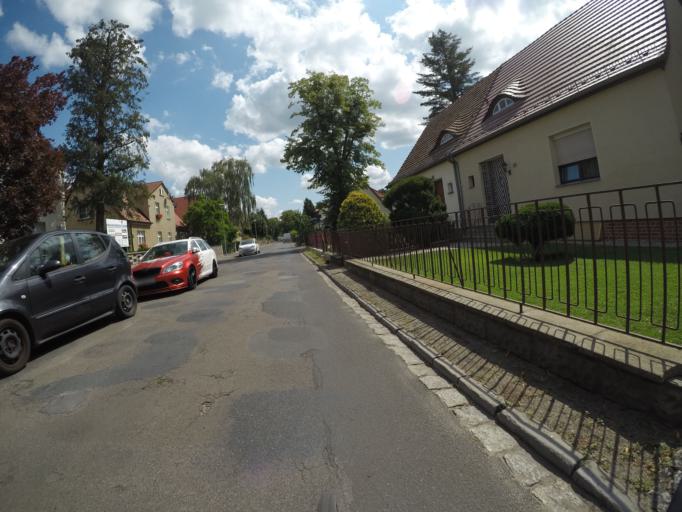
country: DE
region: Brandenburg
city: Potsdam
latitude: 52.3903
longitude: 13.1090
